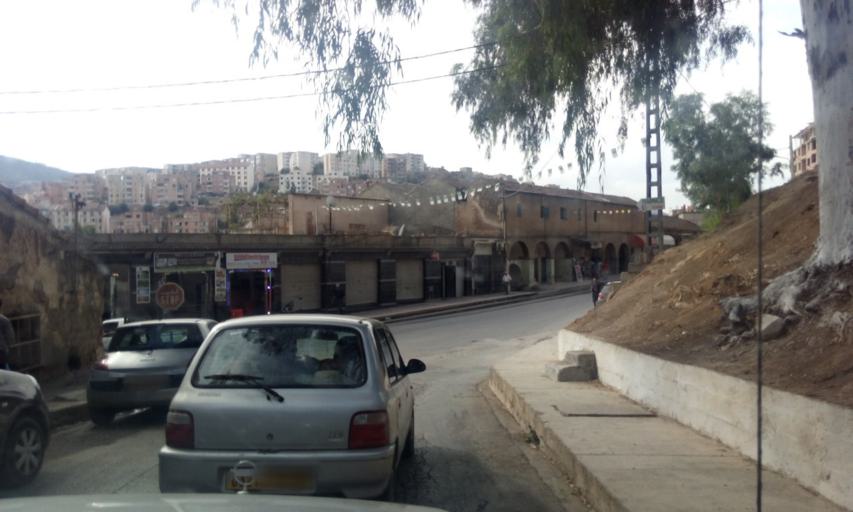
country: DZ
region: Bejaia
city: Seddouk
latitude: 36.6125
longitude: 4.6841
